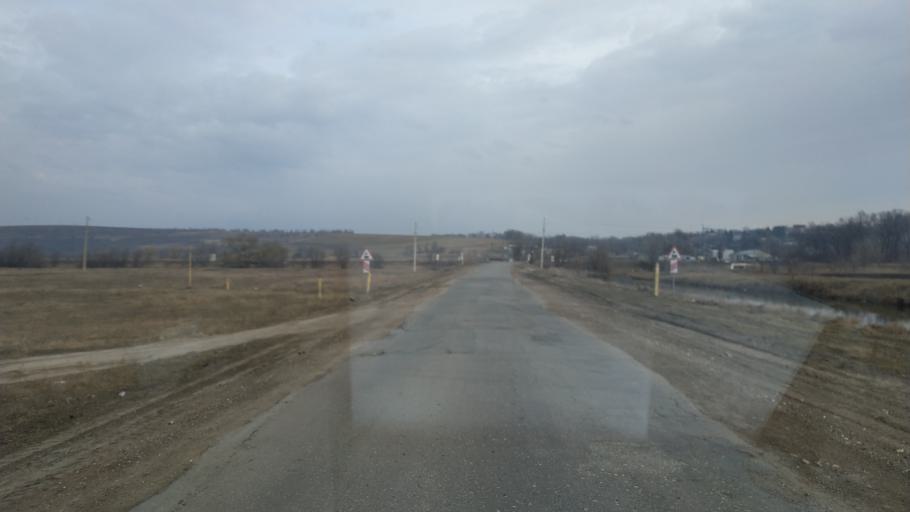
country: MD
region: Chisinau
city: Singera
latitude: 46.9215
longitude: 29.0466
